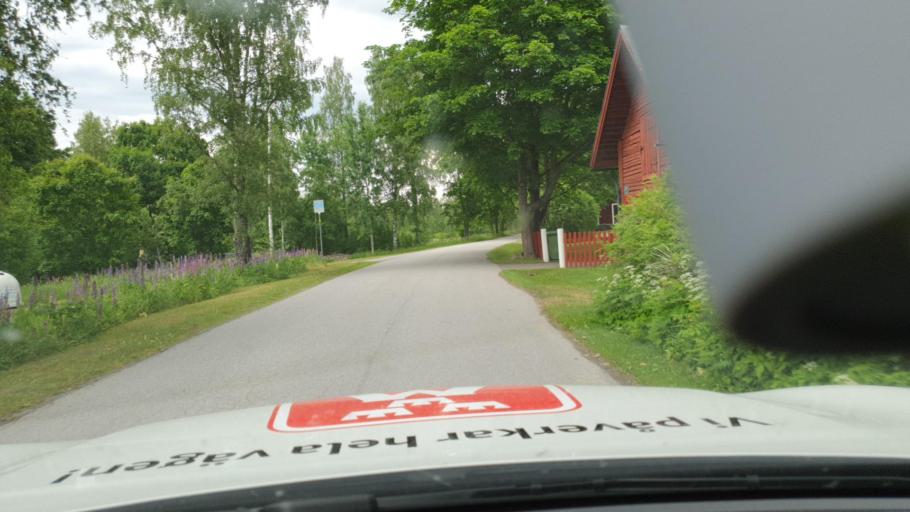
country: SE
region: OErebro
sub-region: Laxa Kommun
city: Laxa
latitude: 58.7733
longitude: 14.5331
